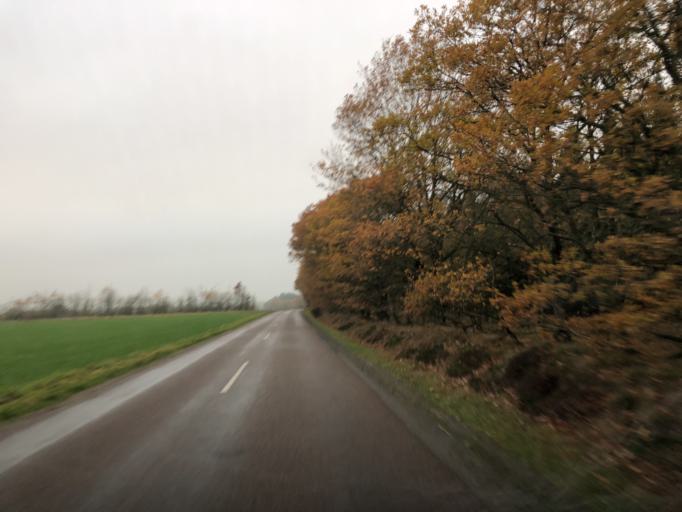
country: DK
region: Central Jutland
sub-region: Herning Kommune
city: Avlum
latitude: 56.2475
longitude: 8.8607
